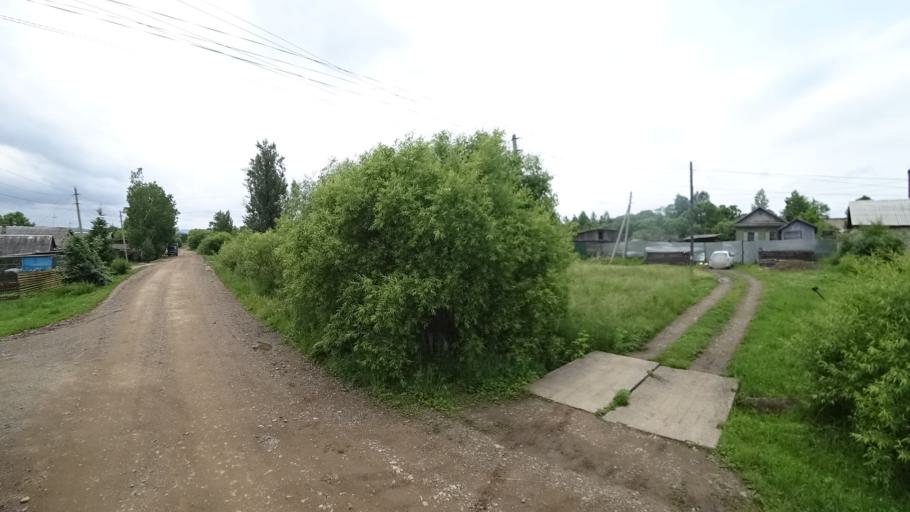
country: RU
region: Primorskiy
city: Novosysoyevka
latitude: 44.2290
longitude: 133.3669
